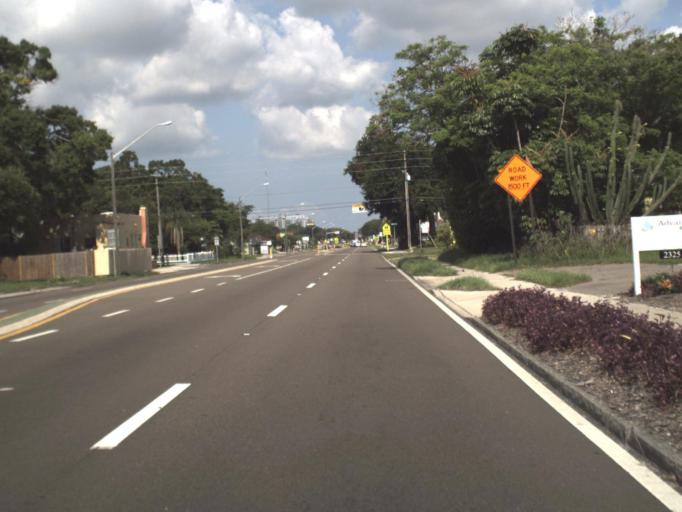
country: US
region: Florida
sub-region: Pinellas County
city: Saint Petersburg
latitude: 27.7775
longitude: -82.6647
